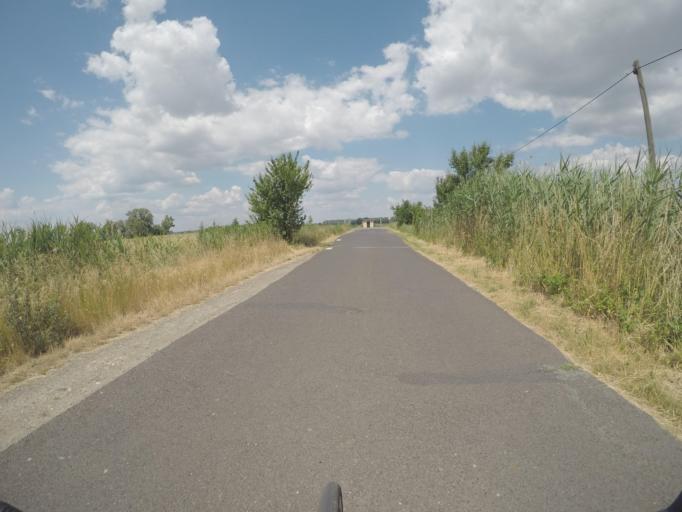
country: DE
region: Brandenburg
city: Roskow
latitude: 52.4481
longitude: 12.6559
